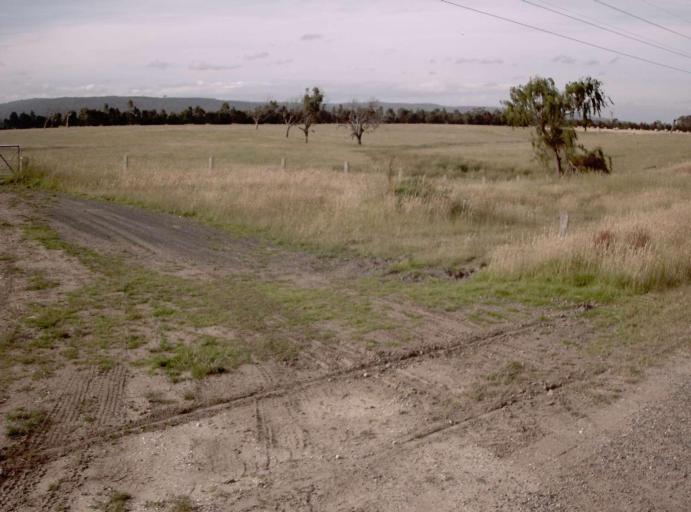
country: AU
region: Victoria
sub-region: Latrobe
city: Traralgon
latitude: -38.1136
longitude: 146.5824
